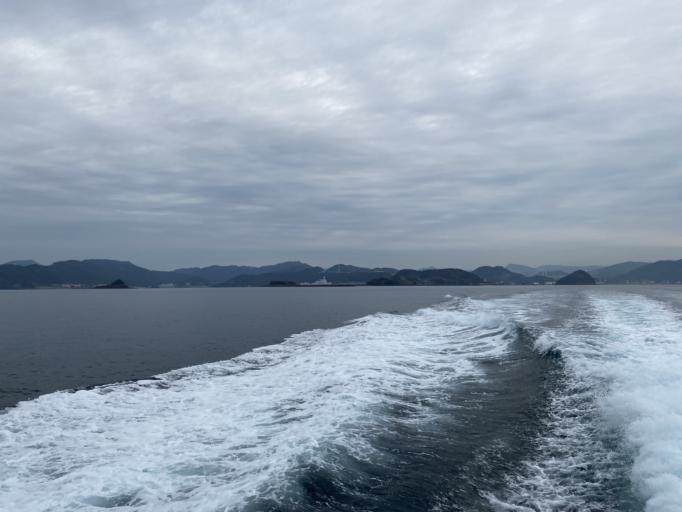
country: JP
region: Nagasaki
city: Nagasaki-shi
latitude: 32.7061
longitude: 129.7990
